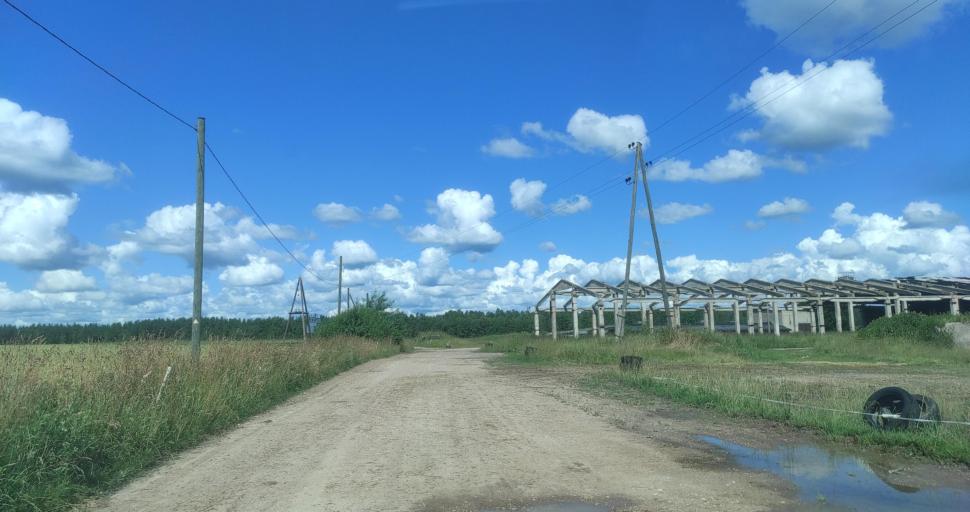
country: LV
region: Kuldigas Rajons
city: Kuldiga
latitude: 57.0017
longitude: 22.1298
